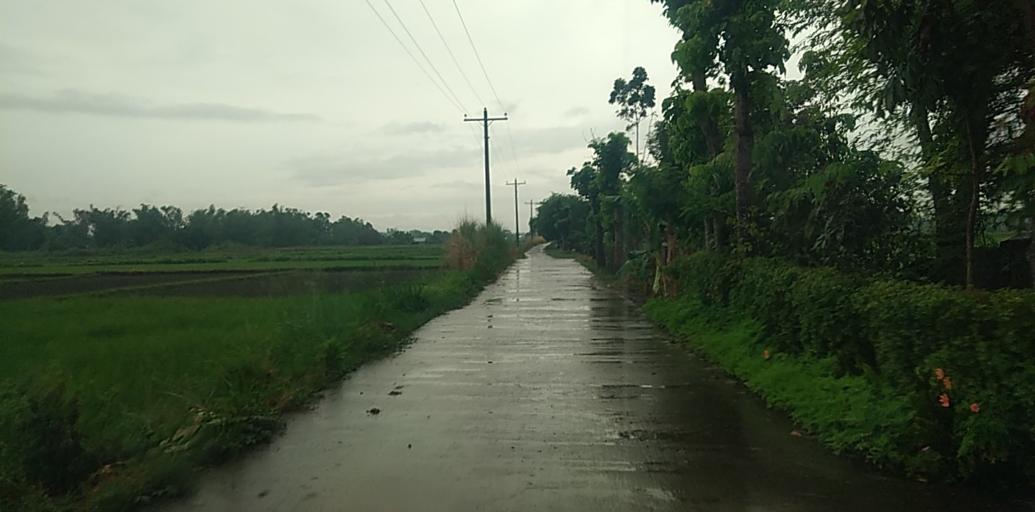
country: PH
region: Central Luzon
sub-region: Province of Pampanga
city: Panlinlang
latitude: 15.1588
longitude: 120.7186
